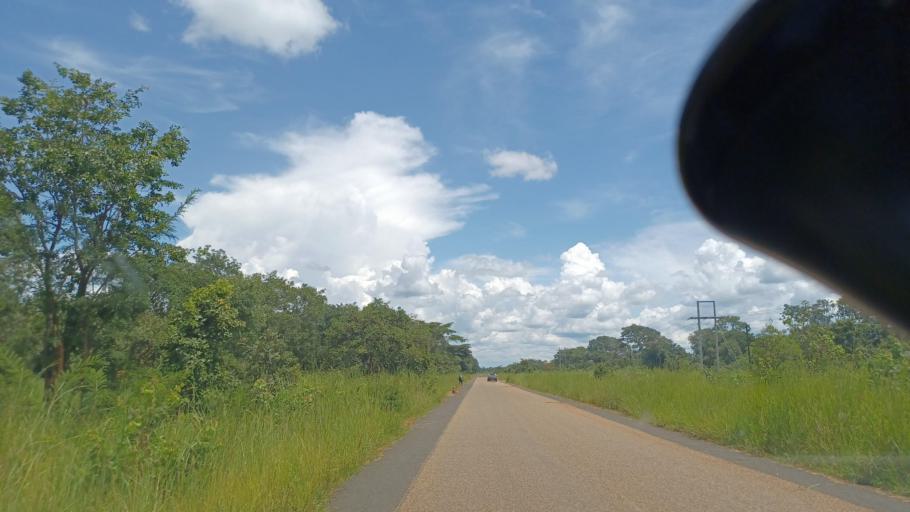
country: ZM
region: North-Western
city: Solwezi
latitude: -12.5685
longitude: 26.1370
